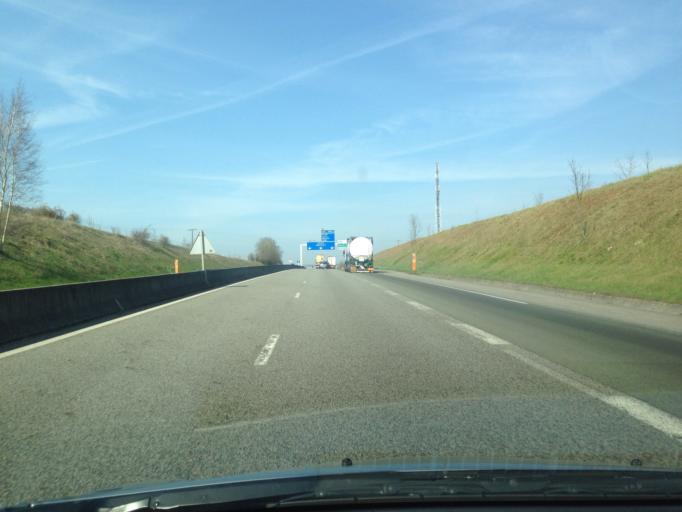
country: FR
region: Haute-Normandie
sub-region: Departement de la Seine-Maritime
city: Neufchatel-en-Bray
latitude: 49.7383
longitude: 1.4705
